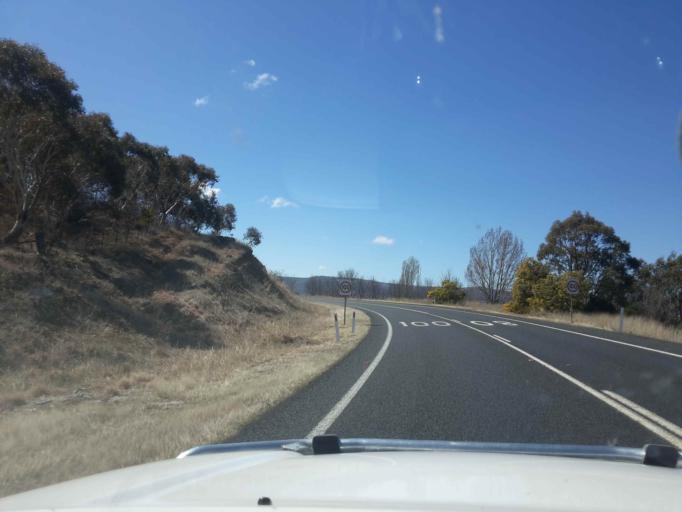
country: AU
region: New South Wales
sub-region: Snowy River
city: Jindabyne
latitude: -36.4081
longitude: 148.5994
